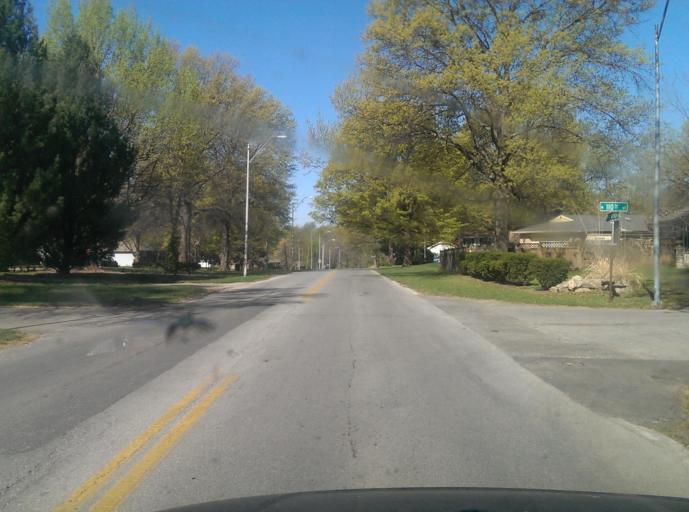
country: US
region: Kansas
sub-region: Johnson County
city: Leawood
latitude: 38.9268
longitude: -94.5969
